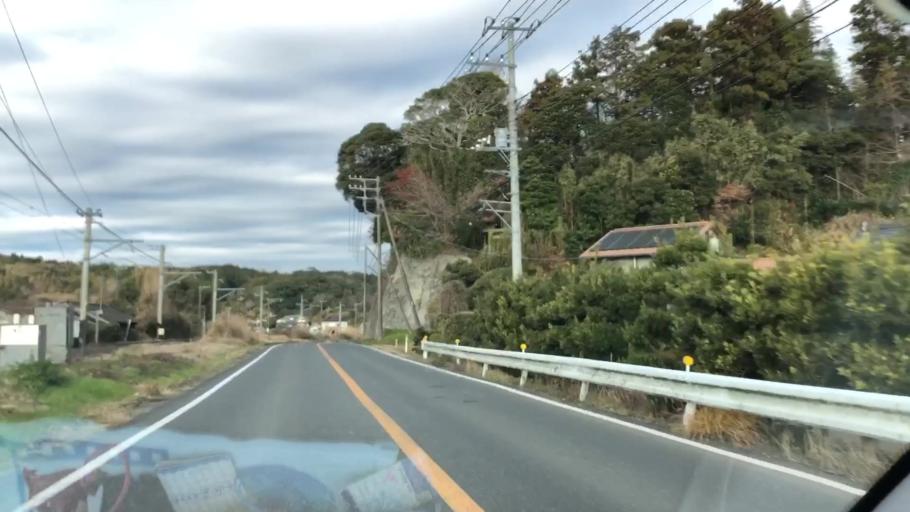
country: JP
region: Chiba
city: Tateyama
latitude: 34.9913
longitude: 139.9230
